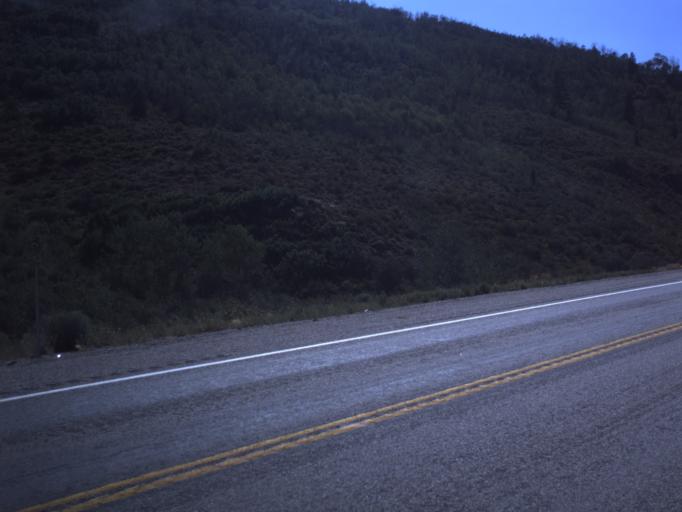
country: US
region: Utah
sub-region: Carbon County
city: Helper
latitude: 40.1926
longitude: -110.9581
